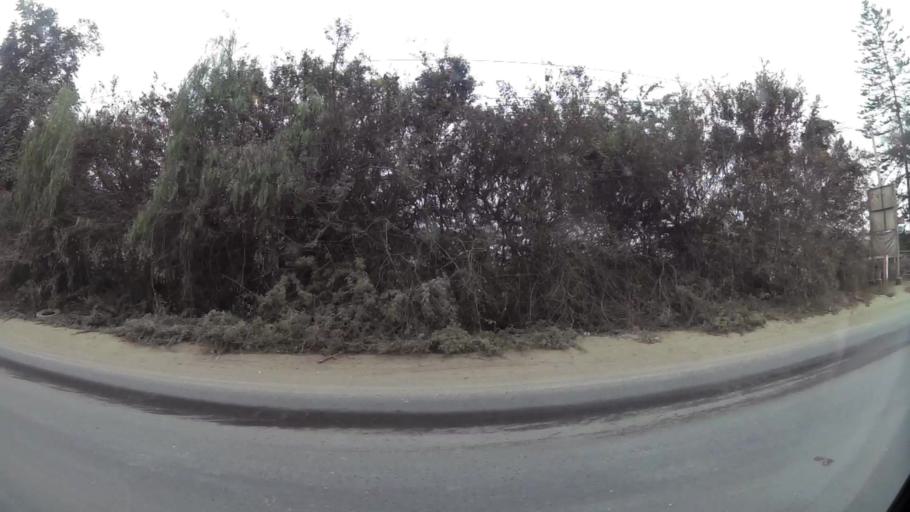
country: PE
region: Lima
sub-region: Lima
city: Punta Hermosa
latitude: -12.2547
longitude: -76.8912
